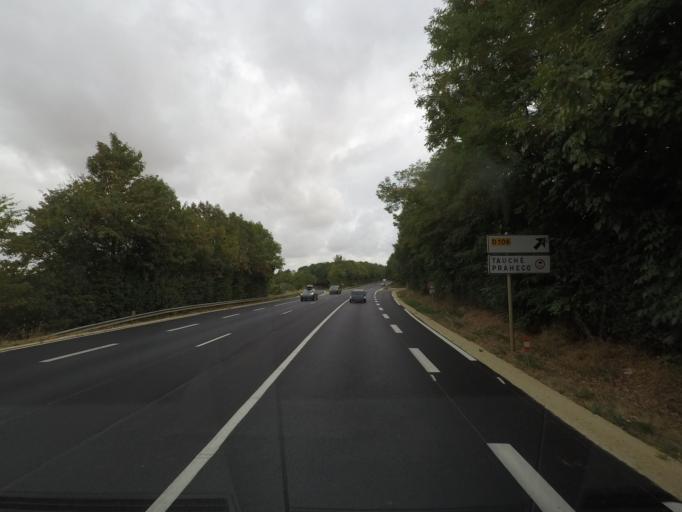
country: FR
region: Poitou-Charentes
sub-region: Departement des Deux-Sevres
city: Celles-sur-Belle
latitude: 46.2609
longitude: -0.2278
